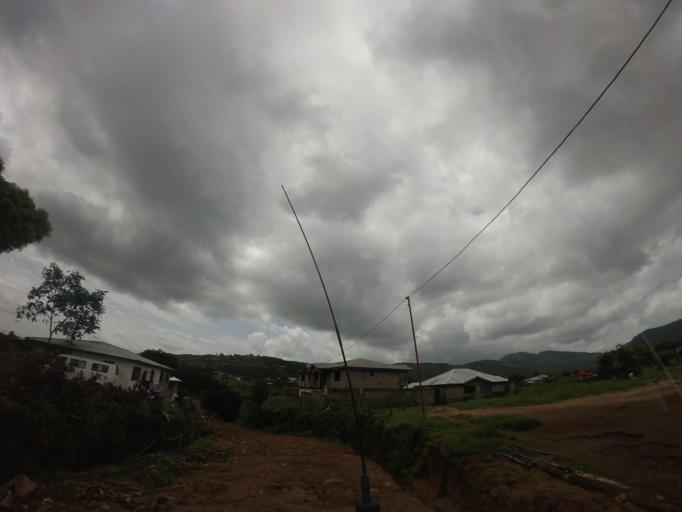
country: SL
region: Western Area
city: Hastings
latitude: 8.3810
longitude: -13.1321
